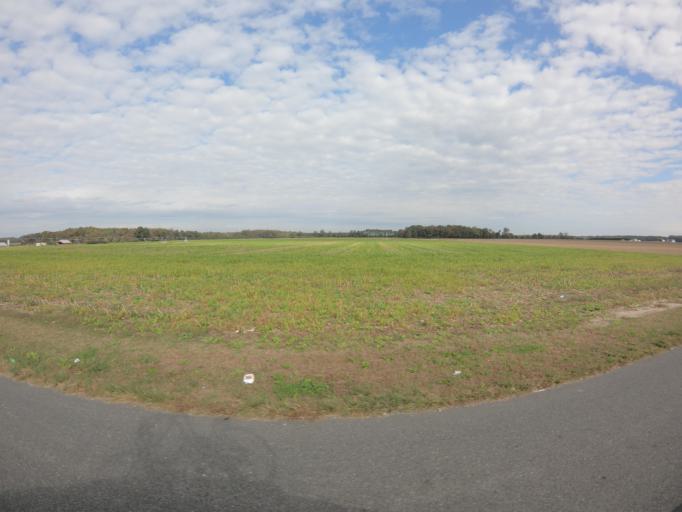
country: US
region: Delaware
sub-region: Sussex County
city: Bridgeville
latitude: 38.7090
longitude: -75.5384
